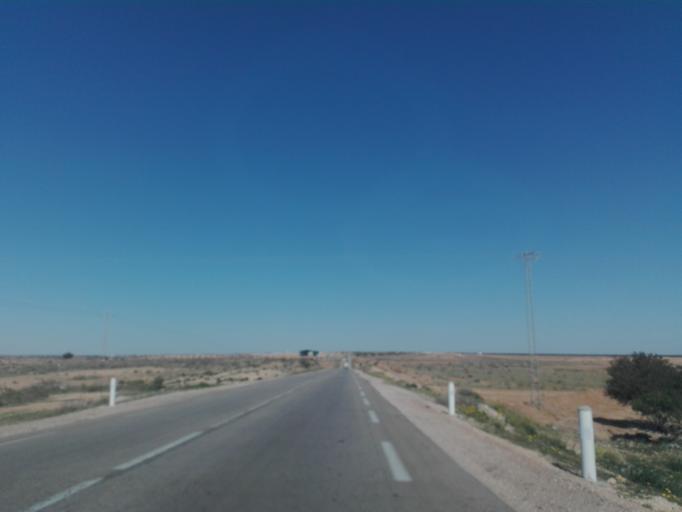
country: TN
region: Safaqis
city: Bi'r `Ali Bin Khalifah
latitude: 34.7309
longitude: 10.4255
